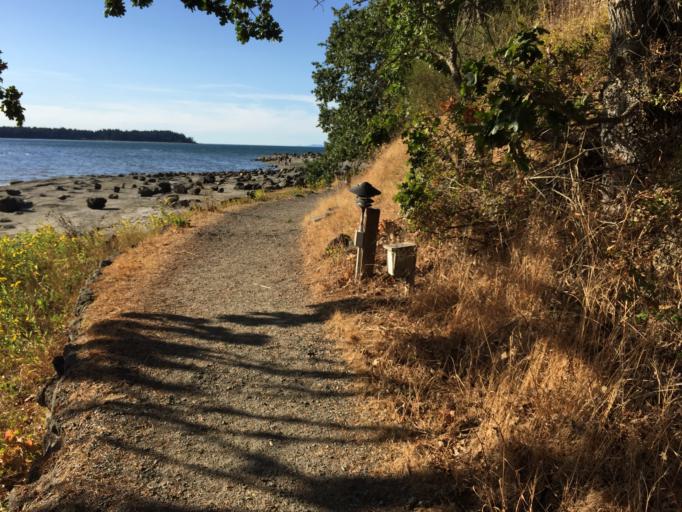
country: CA
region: British Columbia
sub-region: Regional District of Nanaimo
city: Parksville
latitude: 49.3057
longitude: -124.2399
